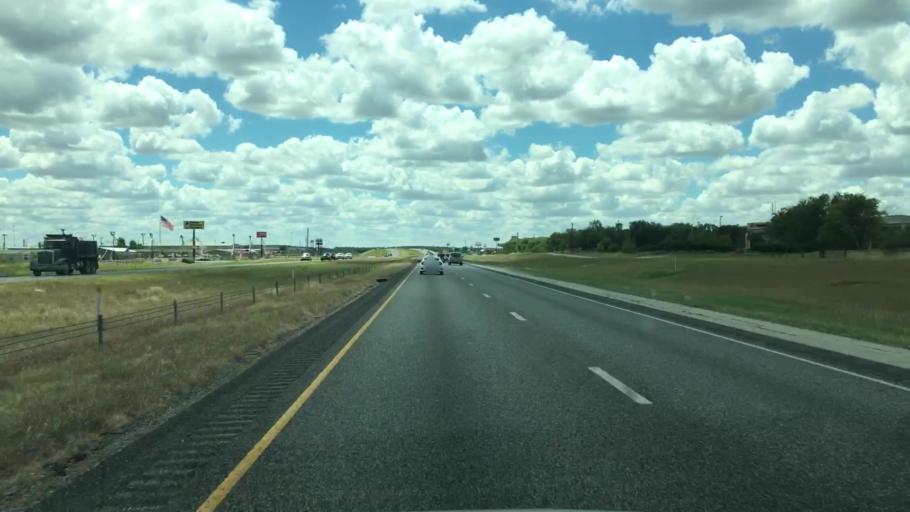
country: US
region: Texas
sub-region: Bexar County
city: Elmendorf
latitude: 29.2275
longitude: -98.4076
